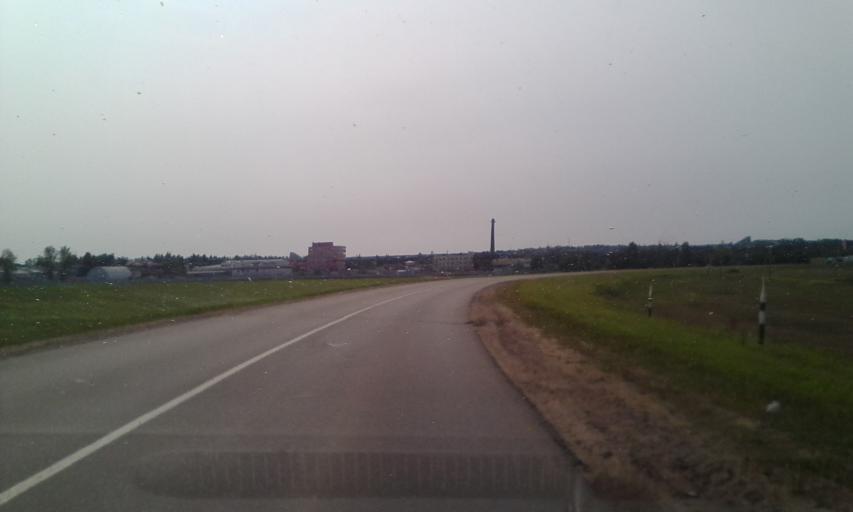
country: BY
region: Minsk
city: Hatava
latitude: 53.7821
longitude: 27.6542
